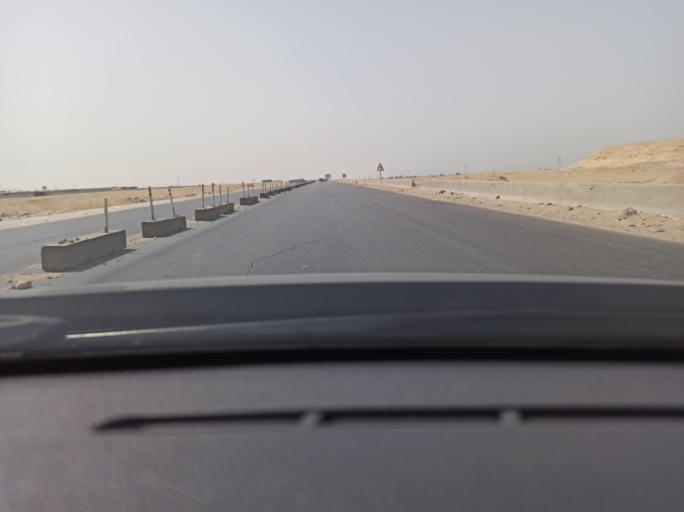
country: EG
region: Muhafazat al Fayyum
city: Al Wasitah
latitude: 29.2845
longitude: 31.2702
